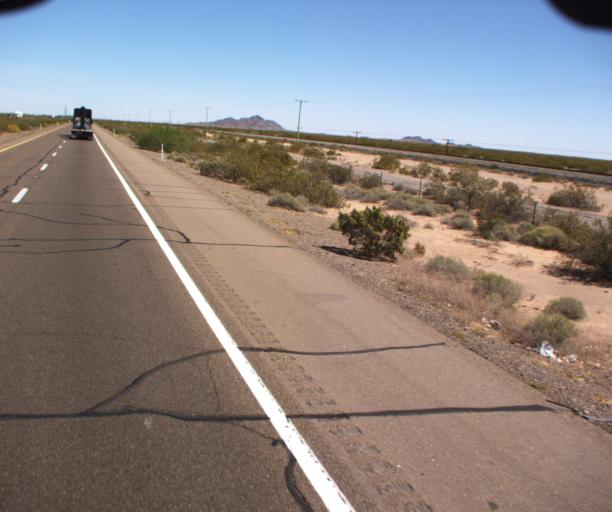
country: US
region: Arizona
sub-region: Yuma County
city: Wellton
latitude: 32.7831
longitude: -113.5762
